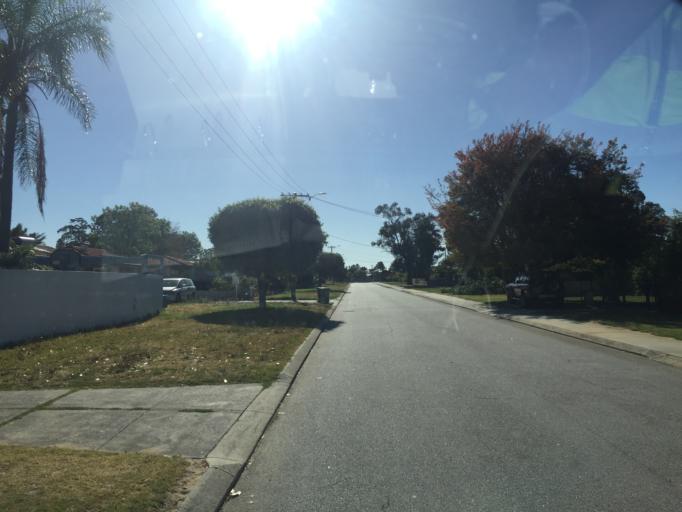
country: AU
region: Western Australia
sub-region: Canning
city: East Cannington
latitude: -32.0151
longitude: 115.9688
